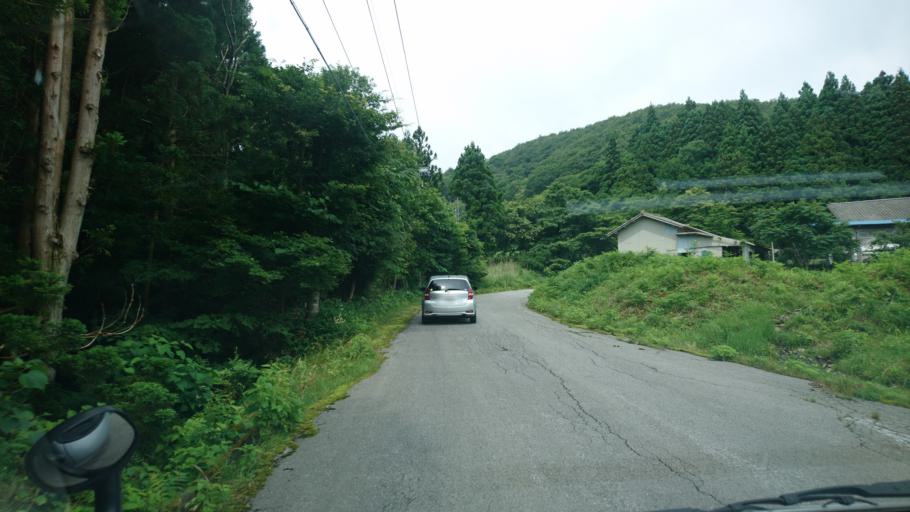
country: JP
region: Iwate
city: Ofunato
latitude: 39.1348
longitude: 141.7609
